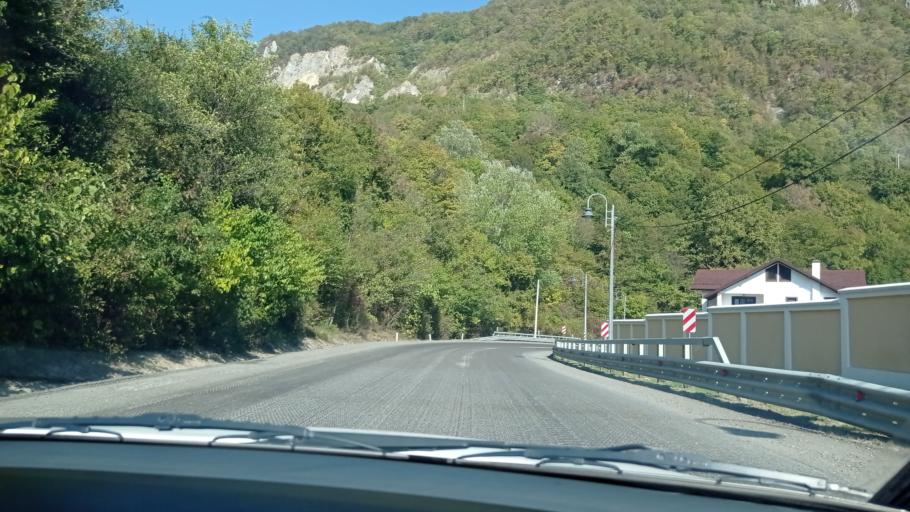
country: RU
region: Krasnodarskiy
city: Vysokoye
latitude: 43.5920
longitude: 40.0081
